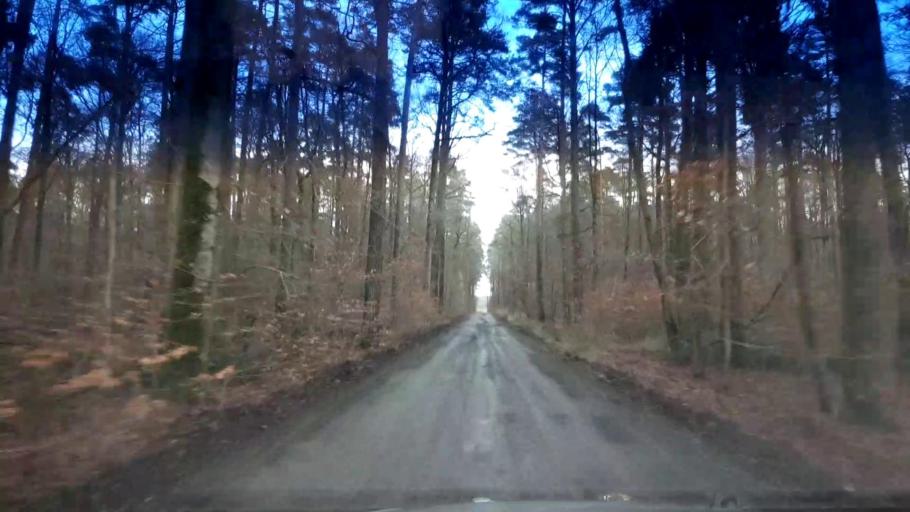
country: DE
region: Bavaria
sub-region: Regierungsbezirk Unterfranken
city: Stettfeld
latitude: 49.9767
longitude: 10.7466
